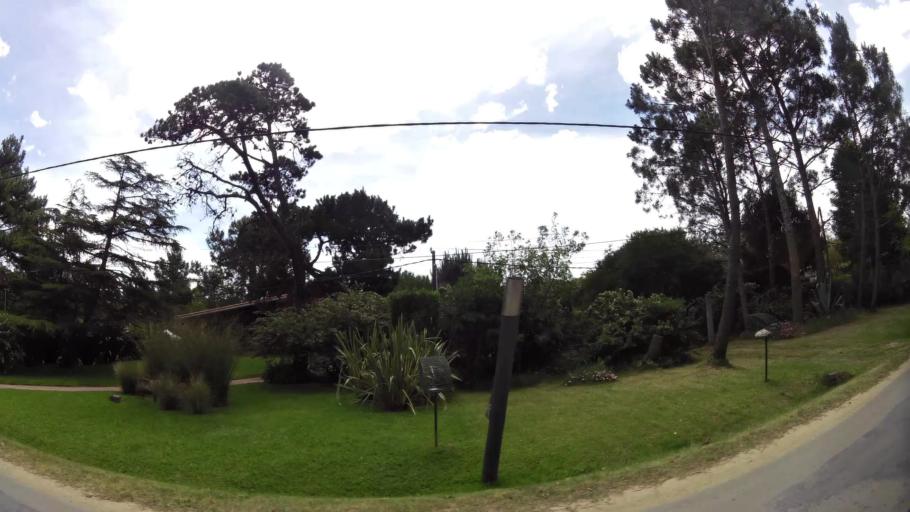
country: UY
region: Canelones
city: Empalme Olmos
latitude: -34.7968
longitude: -55.8876
